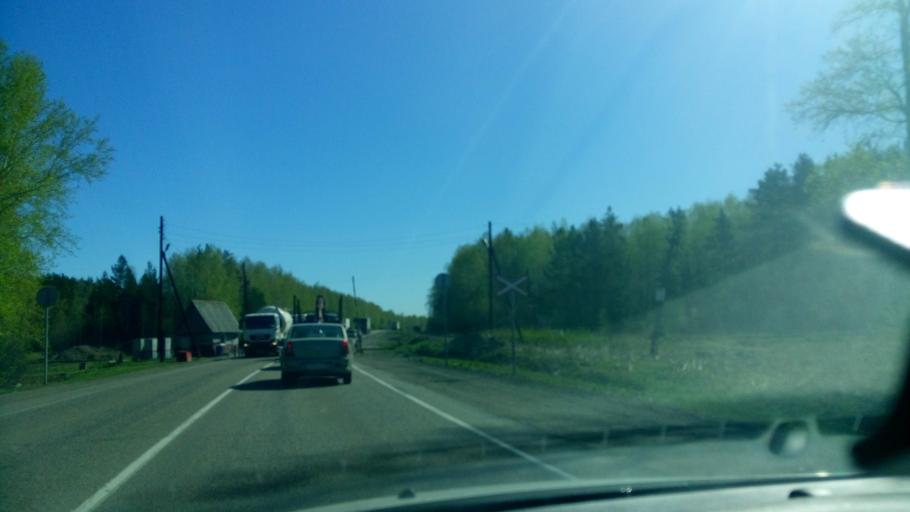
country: RU
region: Sverdlovsk
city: Zarechnyy
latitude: 56.7459
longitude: 61.2891
